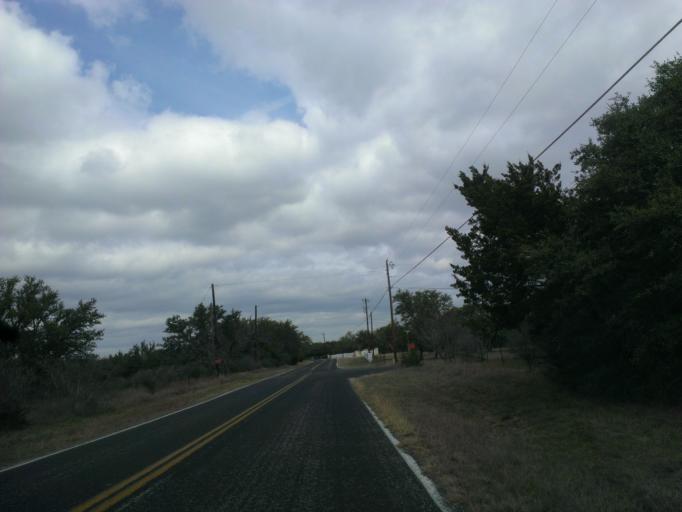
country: US
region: Texas
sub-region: Travis County
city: Briarcliff
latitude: 30.3926
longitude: -98.1045
